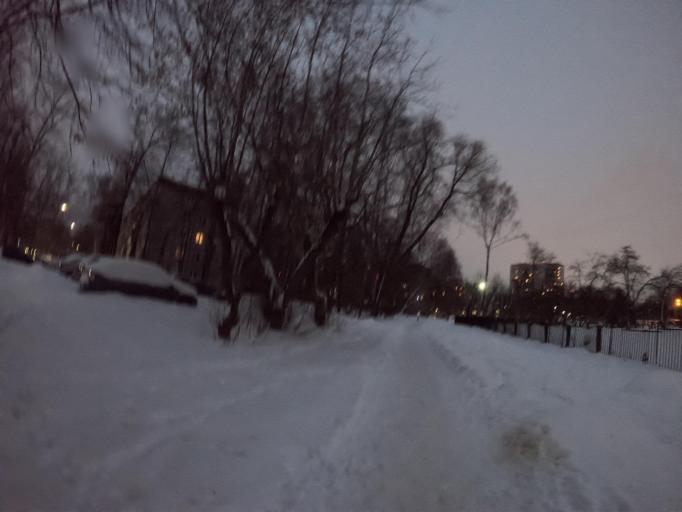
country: RU
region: Moskovskaya
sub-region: Podol'skiy Rayon
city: Podol'sk
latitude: 55.4213
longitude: 37.5224
